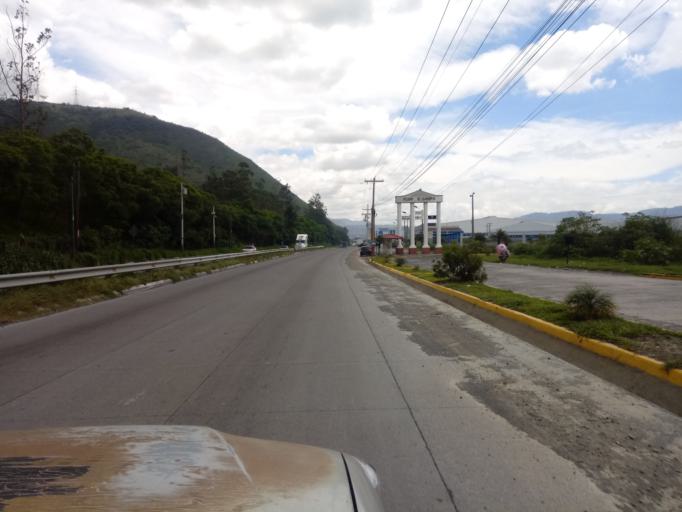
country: GT
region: Escuintla
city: San Vicente Pacaya
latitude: 14.4497
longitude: -90.6439
